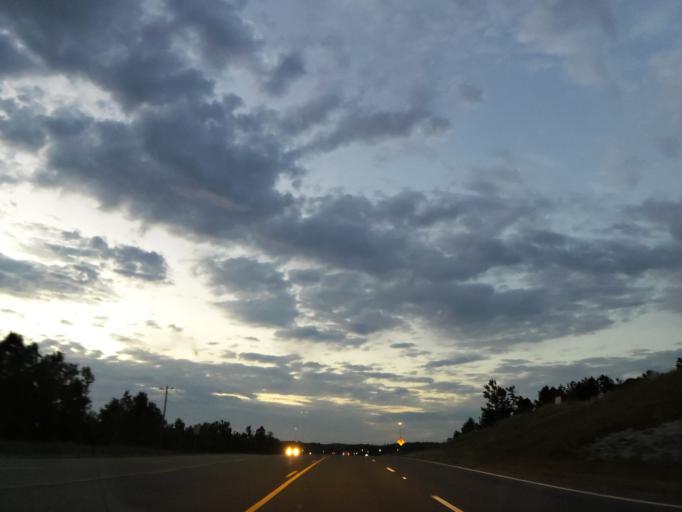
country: US
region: Alabama
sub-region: Marion County
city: Winfield
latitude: 33.9826
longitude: -87.7756
